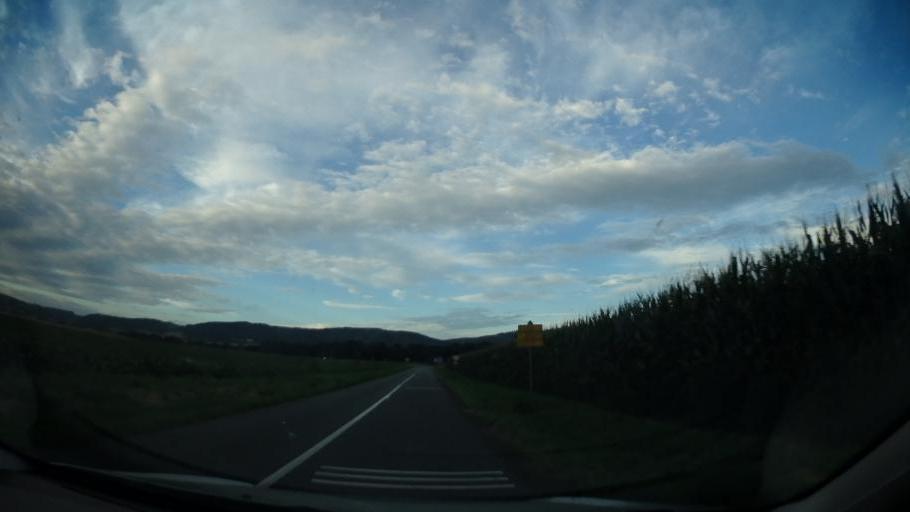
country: CZ
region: Olomoucky
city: Ujezd
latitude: 49.7855
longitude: 17.1869
